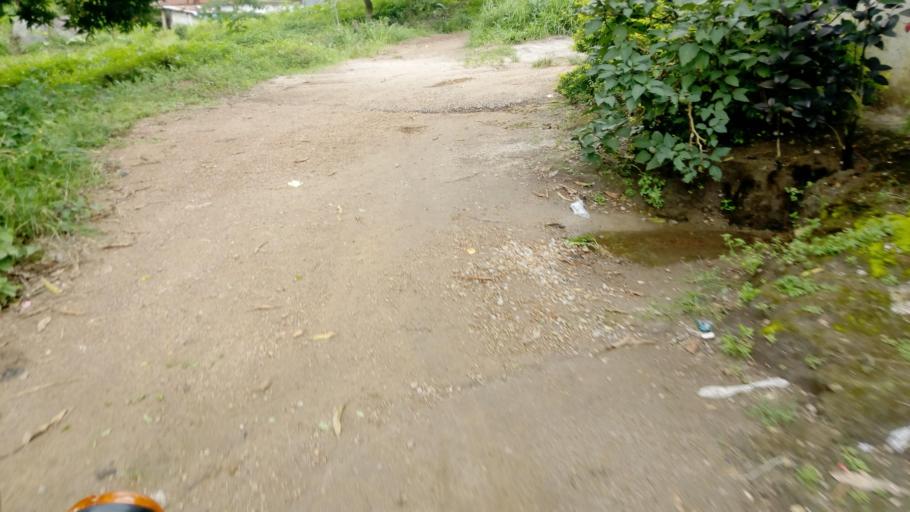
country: SL
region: Northern Province
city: Makeni
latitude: 8.8904
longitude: -12.0294
